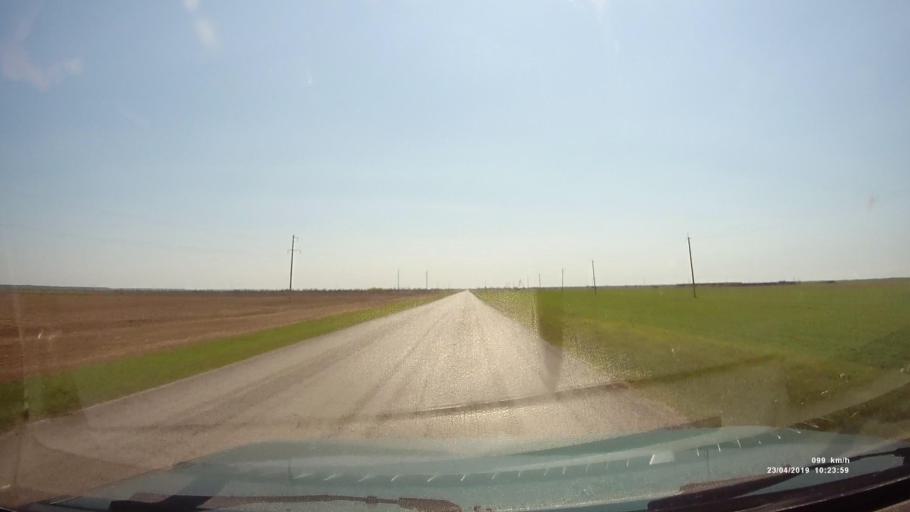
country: RU
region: Rostov
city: Sovetskoye
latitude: 46.6429
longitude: 42.4337
